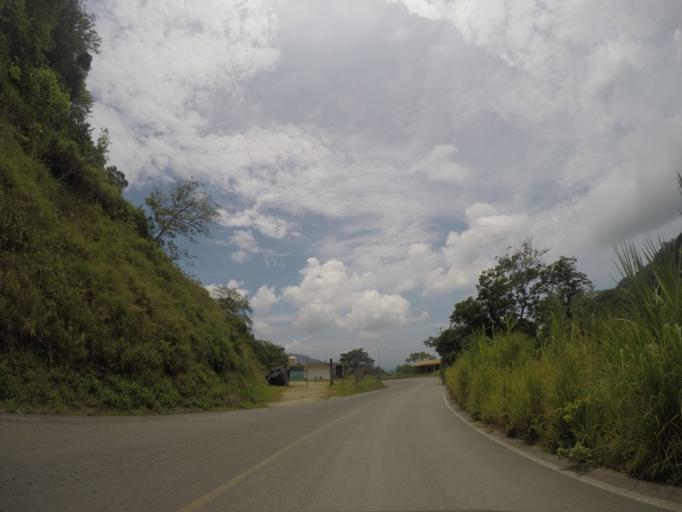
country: MX
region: Oaxaca
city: Pluma Hidalgo
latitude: 15.9080
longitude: -96.4196
